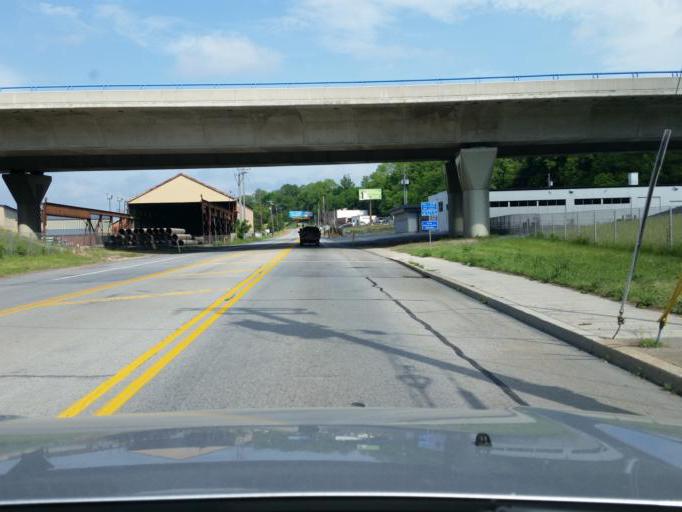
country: US
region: Pennsylvania
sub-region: Dauphin County
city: Highspire
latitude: 40.2119
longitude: -76.7969
